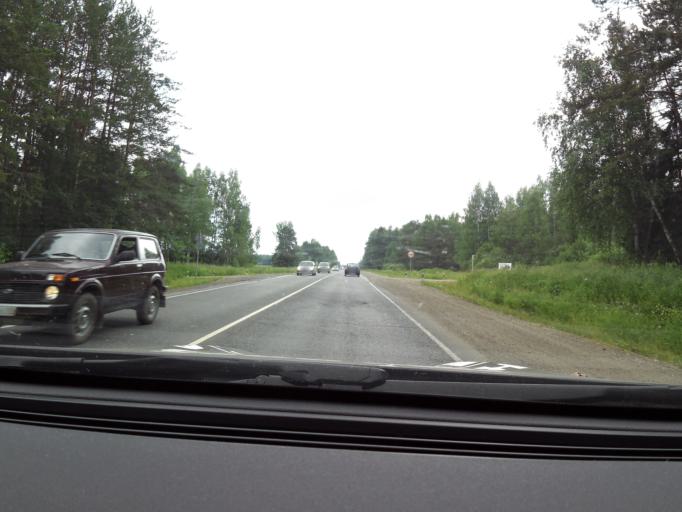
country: RU
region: Perm
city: Kungur
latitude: 57.4421
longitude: 56.8167
